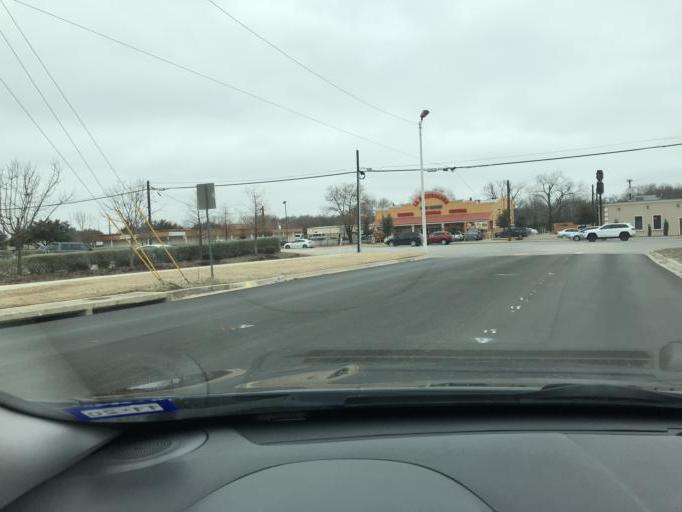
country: US
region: Texas
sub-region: Denton County
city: Denton
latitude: 33.2285
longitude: -97.1550
